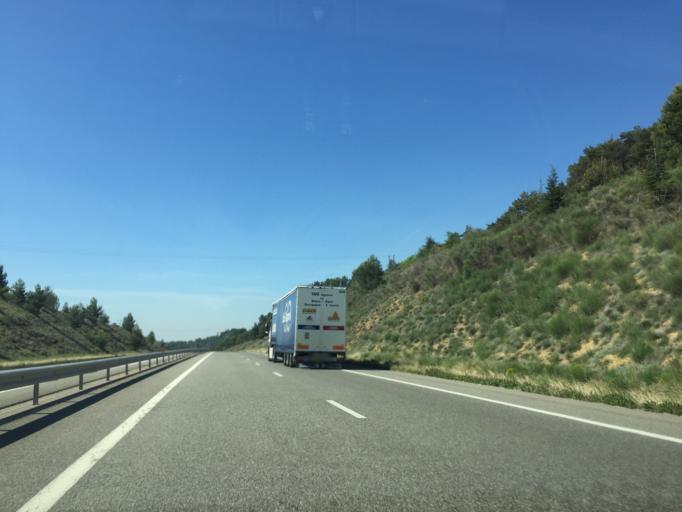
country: FR
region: Provence-Alpes-Cote d'Azur
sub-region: Departement des Alpes-de-Haute-Provence
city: Volonne
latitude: 44.0810
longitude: 5.9831
